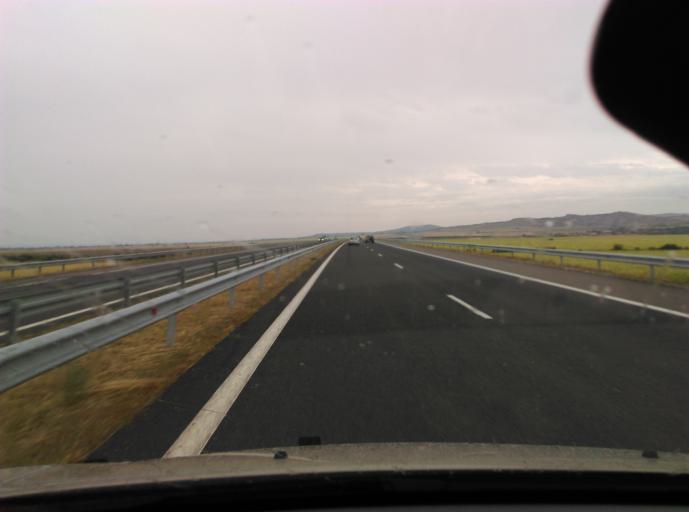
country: BG
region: Sliven
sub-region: Obshtina Nova Zagora
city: Nova Zagora
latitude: 42.4386
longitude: 25.9926
